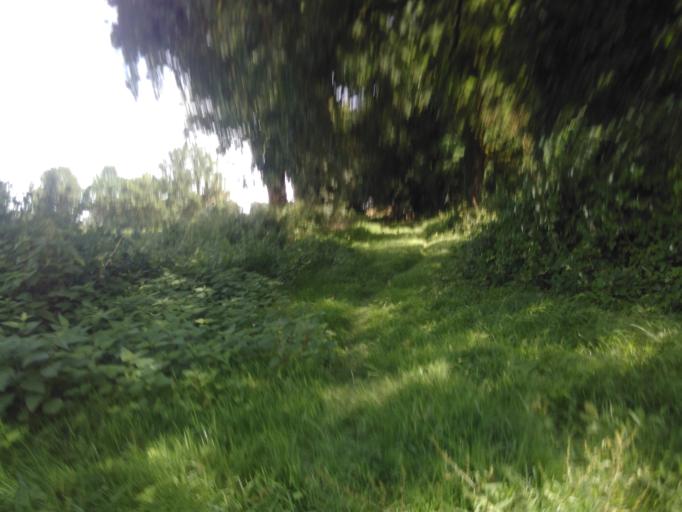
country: FR
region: Pays de la Loire
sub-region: Departement de la Vendee
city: La Ferriere
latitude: 46.7097
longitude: -1.3038
